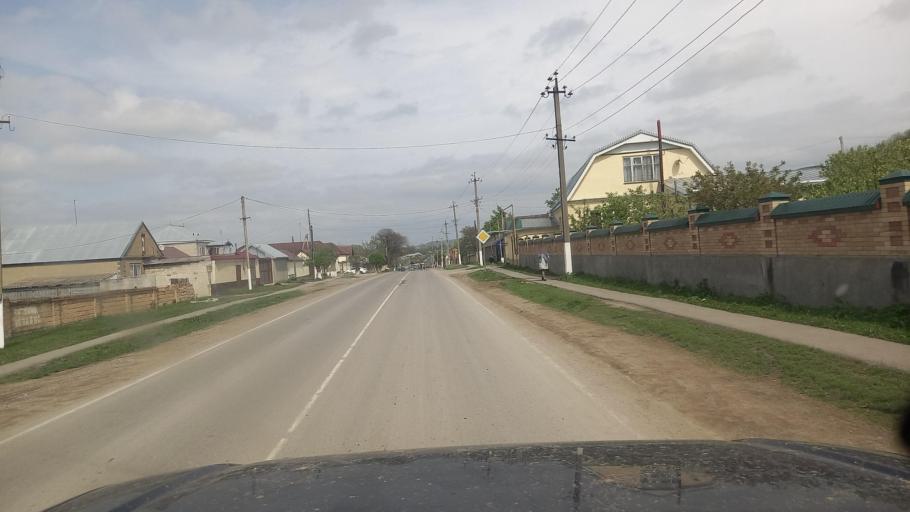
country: RU
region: Kabardino-Balkariya
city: Sarmakovo
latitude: 43.7315
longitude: 43.1694
